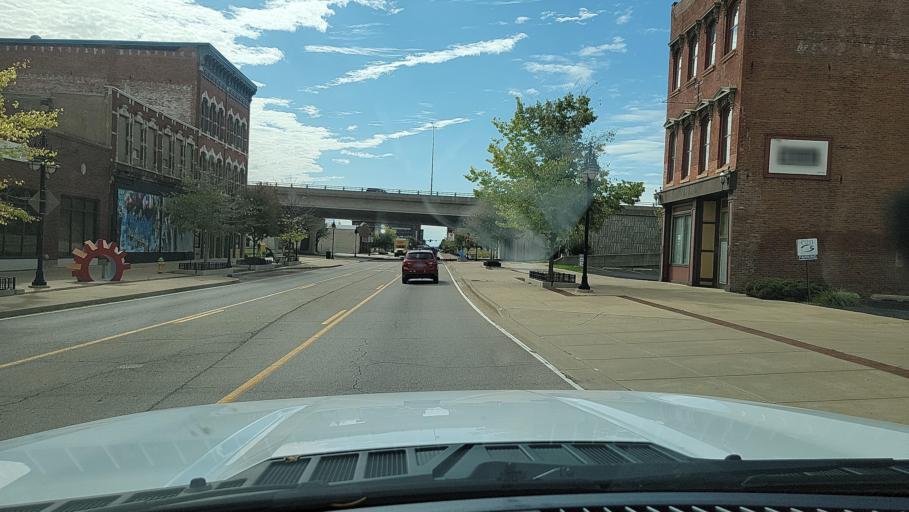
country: US
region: Illinois
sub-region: Peoria County
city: Peoria
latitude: 40.6882
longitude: -89.5927
